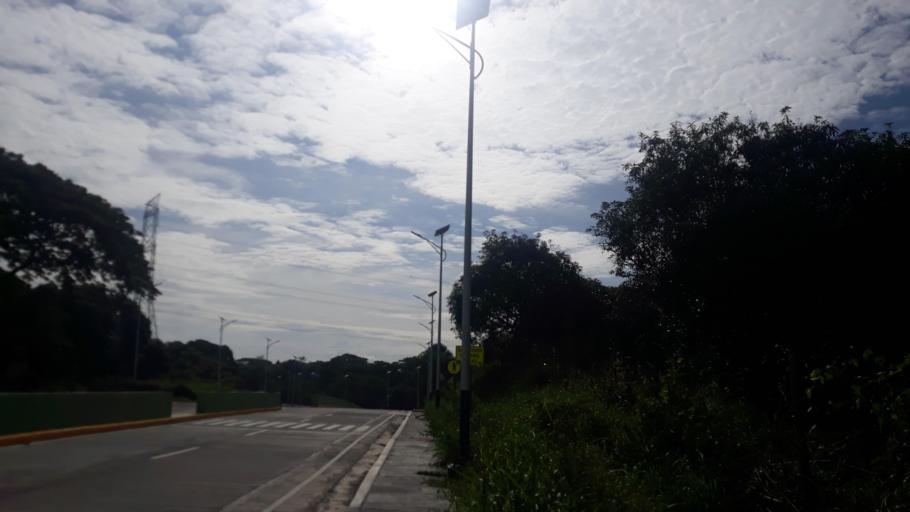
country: PH
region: Calabarzon
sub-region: Province of Cavite
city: Bulihan
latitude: 14.2897
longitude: 120.9664
